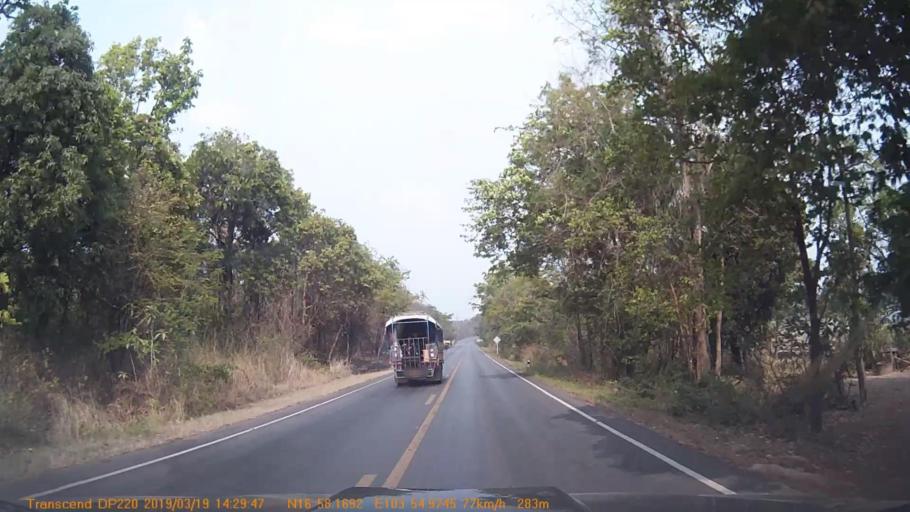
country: TH
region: Sakon Nakhon
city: Phu Phan
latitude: 16.9697
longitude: 103.9167
